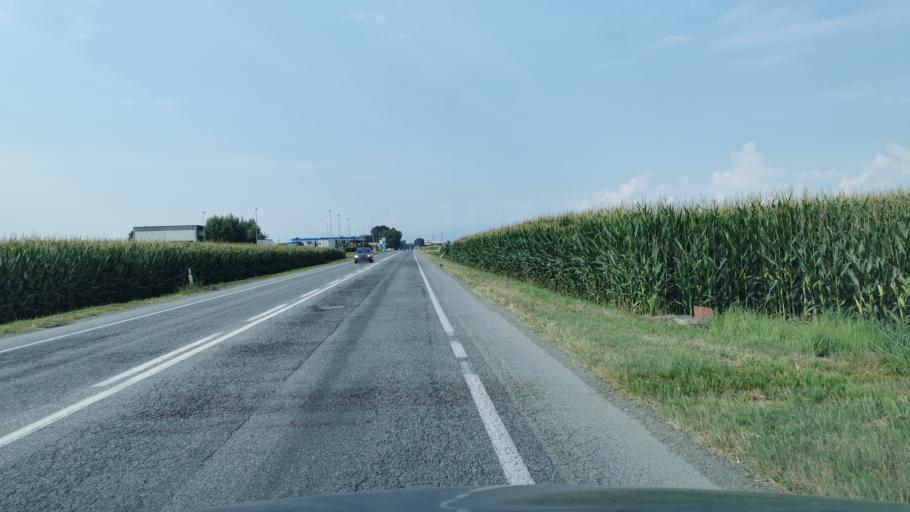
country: IT
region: Piedmont
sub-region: Provincia di Torino
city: Vigone
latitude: 44.8501
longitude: 7.5082
